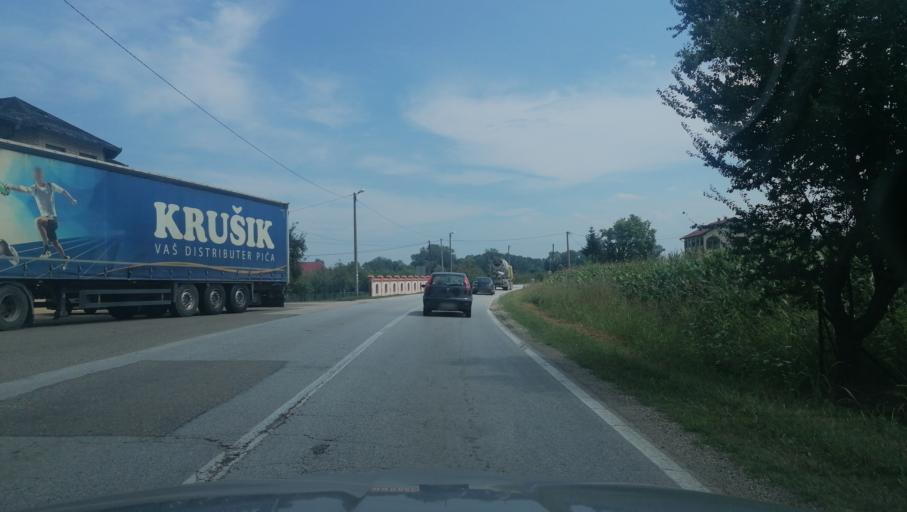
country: HR
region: Vukovarsko-Srijemska
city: Soljani
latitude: 44.8312
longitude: 19.0258
